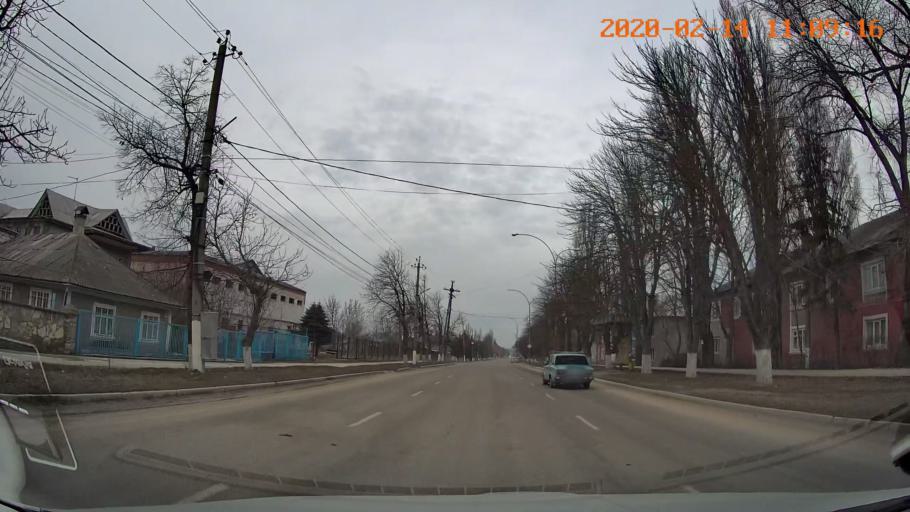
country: MD
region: Raionul Edinet
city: Edinet
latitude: 48.1770
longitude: 27.2954
